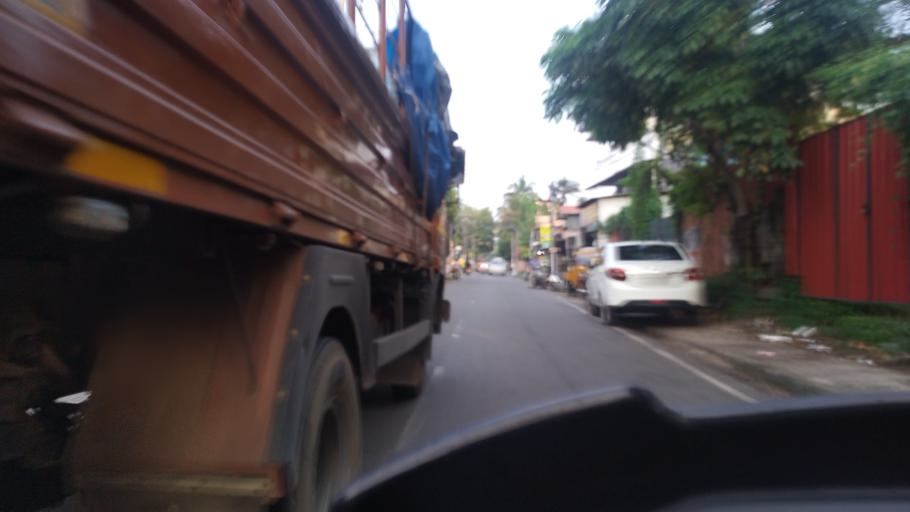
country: IN
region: Kerala
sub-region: Ernakulam
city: Elur
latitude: 10.0197
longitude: 76.2969
